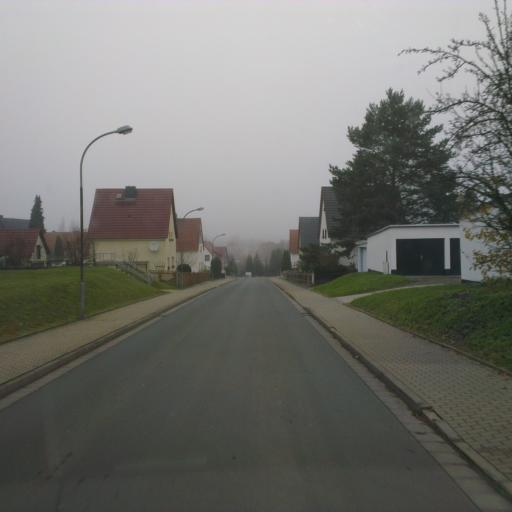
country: DE
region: Thuringia
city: Kahla
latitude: 50.8084
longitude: 11.5828
